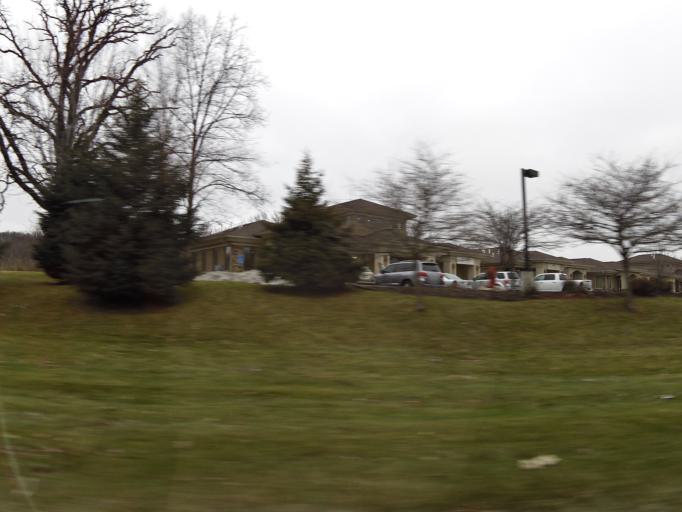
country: US
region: Minnesota
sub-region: Scott County
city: Prior Lake
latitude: 44.7466
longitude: -93.3905
